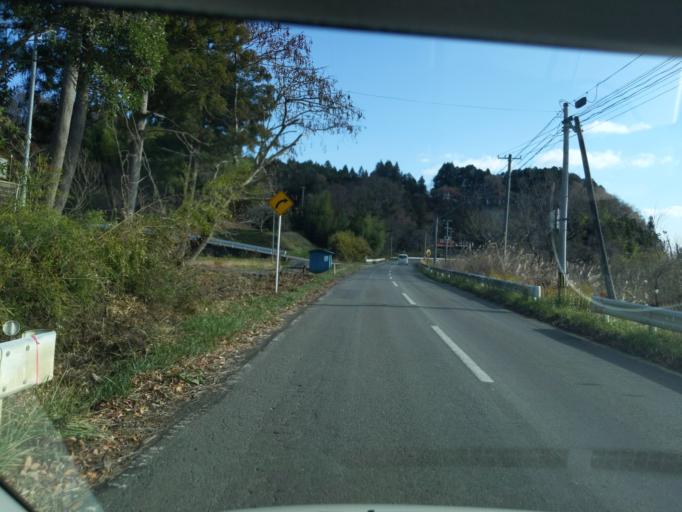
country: JP
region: Miyagi
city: Kogota
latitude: 38.7266
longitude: 141.0796
